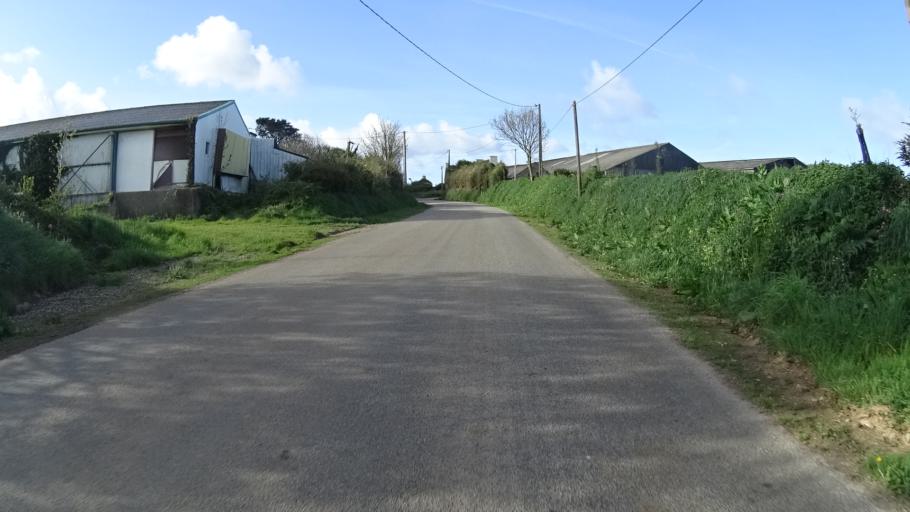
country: FR
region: Brittany
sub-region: Departement du Finistere
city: Plouzane
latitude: 48.3973
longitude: -4.6649
